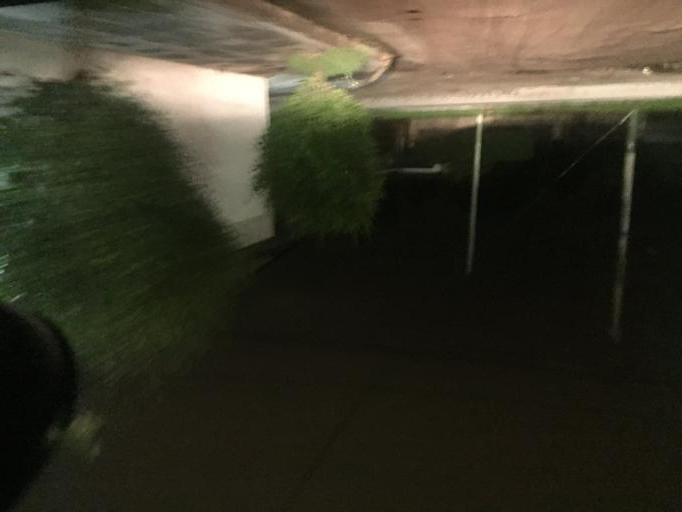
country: AR
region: Cordoba
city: Villa Allende
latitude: -31.3015
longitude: -64.2878
